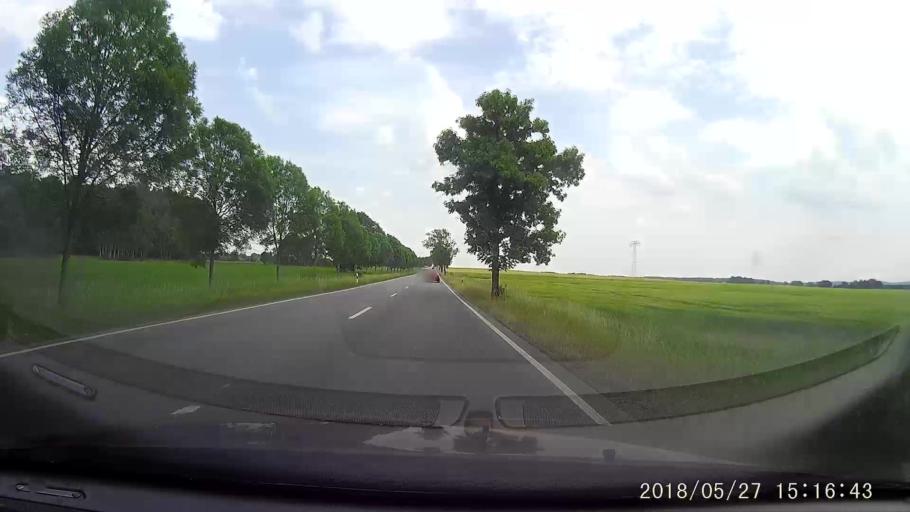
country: DE
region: Saxony
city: Niesky
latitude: 51.2758
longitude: 14.8285
